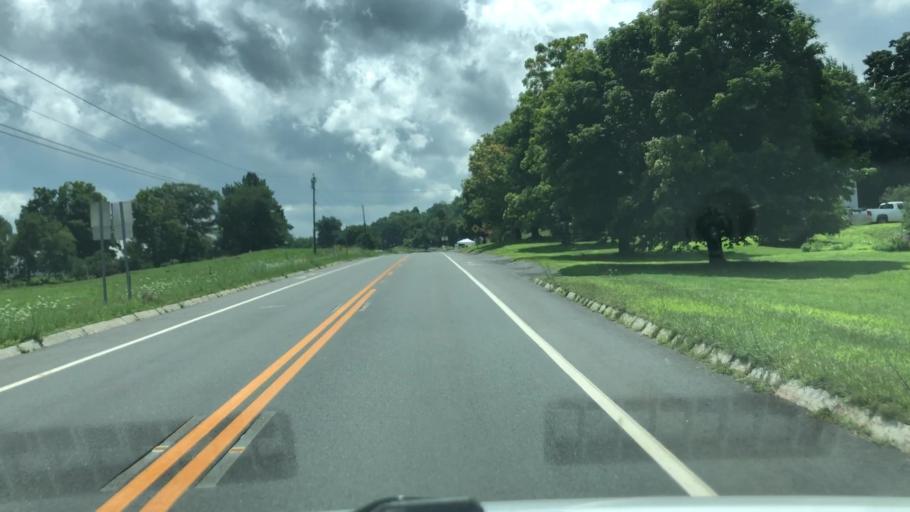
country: US
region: Massachusetts
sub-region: Franklin County
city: Ashfield
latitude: 42.5278
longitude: -72.8067
